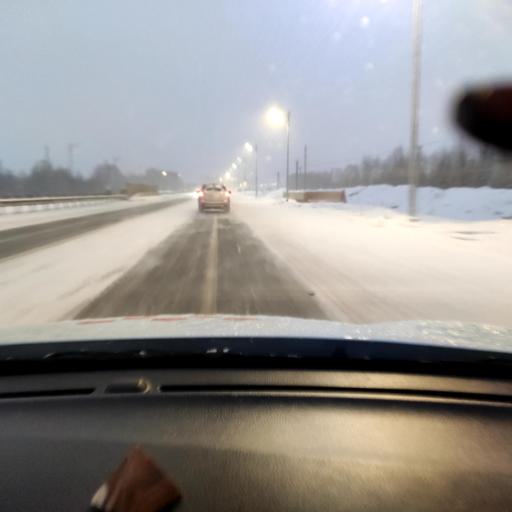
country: RU
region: Tatarstan
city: Stolbishchi
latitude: 55.6461
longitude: 49.2909
